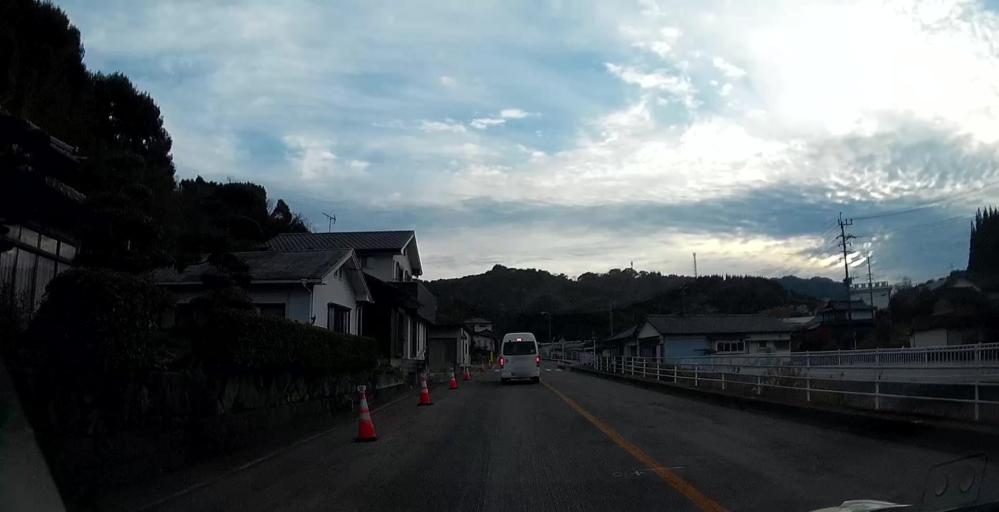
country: JP
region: Kumamoto
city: Yatsushiro
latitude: 32.4989
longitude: 130.4241
